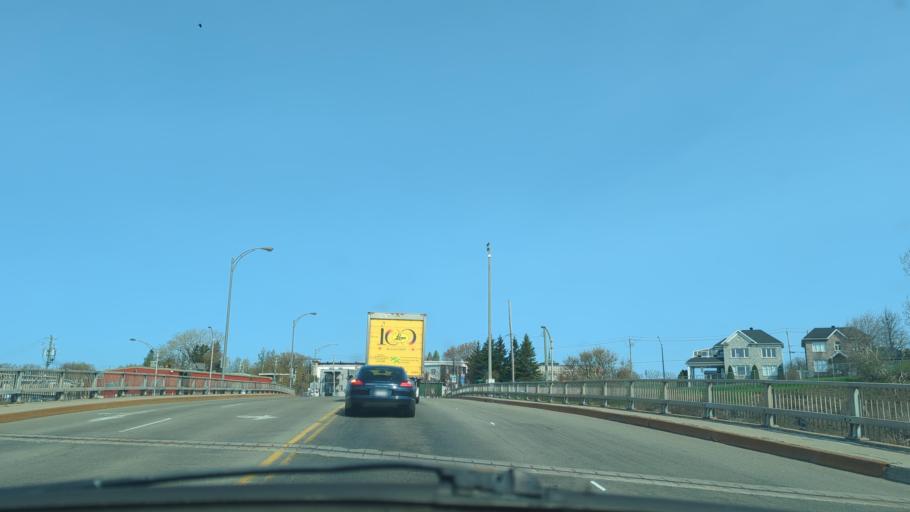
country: CA
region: Quebec
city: Quebec
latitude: 46.8531
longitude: -71.2263
